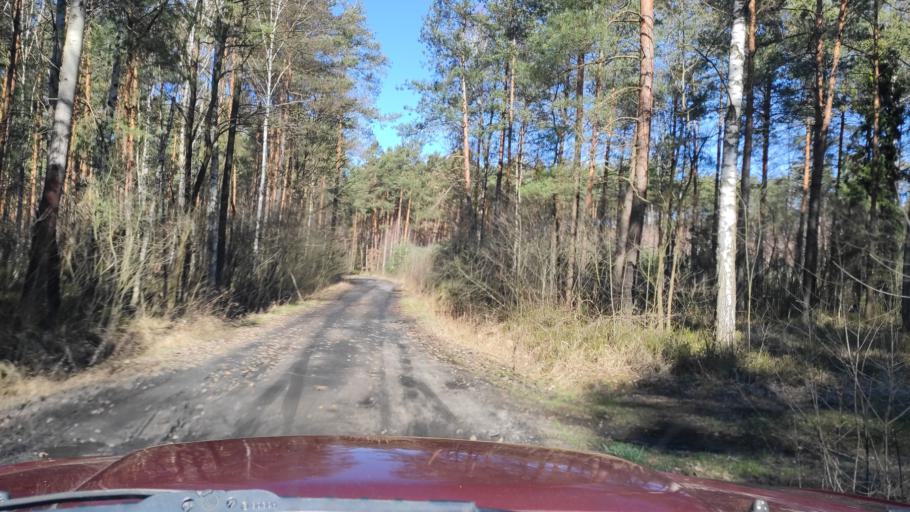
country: PL
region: Masovian Voivodeship
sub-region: Powiat kozienicki
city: Garbatka-Letnisko
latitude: 51.4343
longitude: 21.5467
